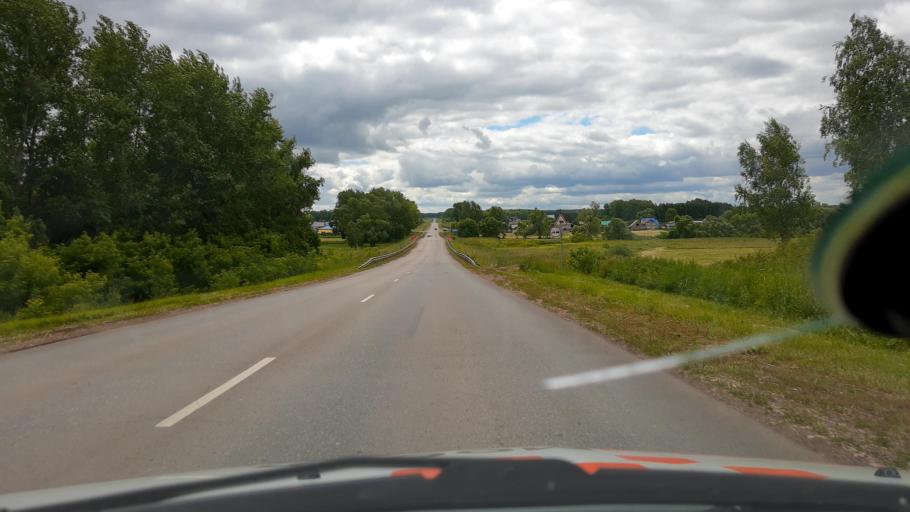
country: RU
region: Bashkortostan
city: Buzdyak
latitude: 54.6924
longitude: 54.5580
